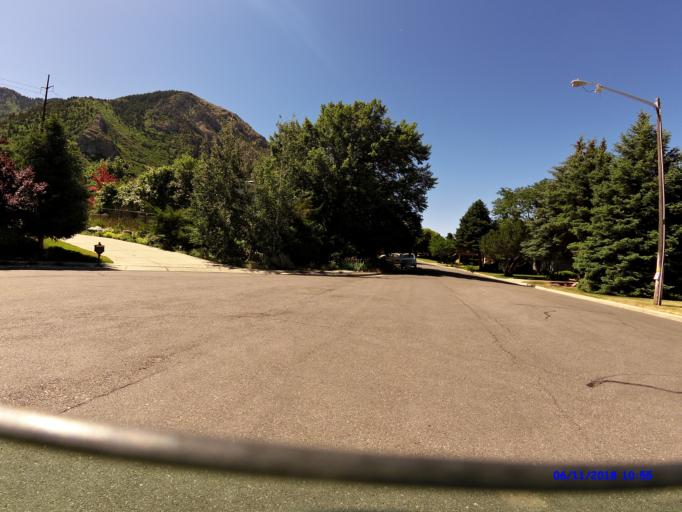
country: US
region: Utah
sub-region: Weber County
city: Ogden
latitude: 41.2178
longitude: -111.9298
